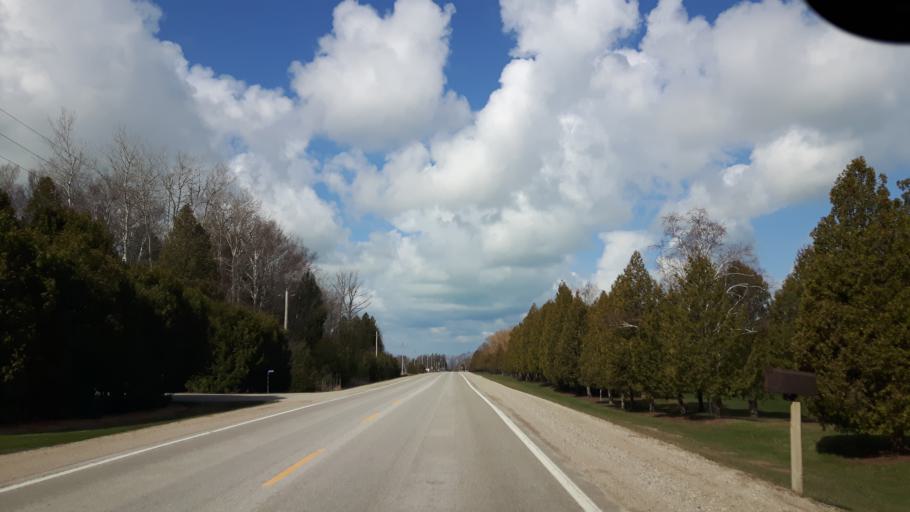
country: CA
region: Ontario
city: Bluewater
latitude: 43.5871
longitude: -81.6955
